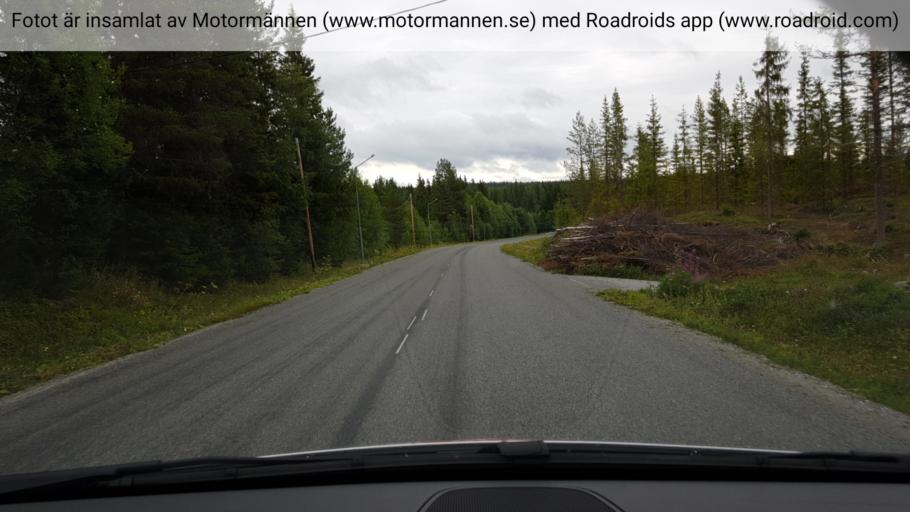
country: SE
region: Jaemtland
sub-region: Krokoms Kommun
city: Krokom
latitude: 63.6753
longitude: 14.5678
